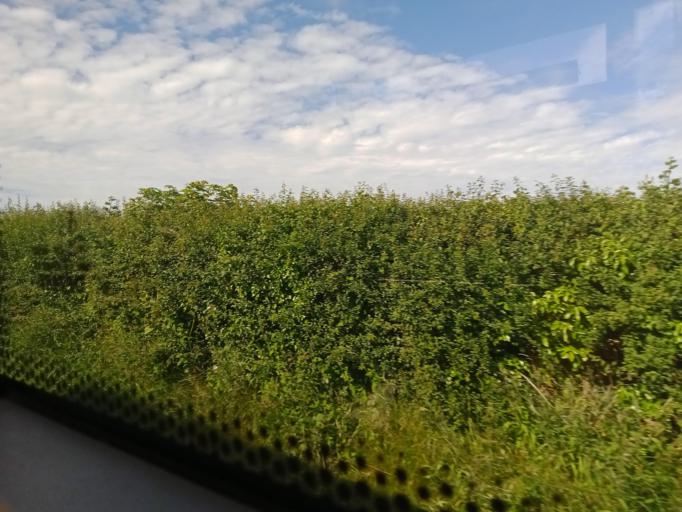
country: GB
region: Wales
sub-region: Anglesey
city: Llangoed
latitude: 53.3037
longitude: -4.0790
